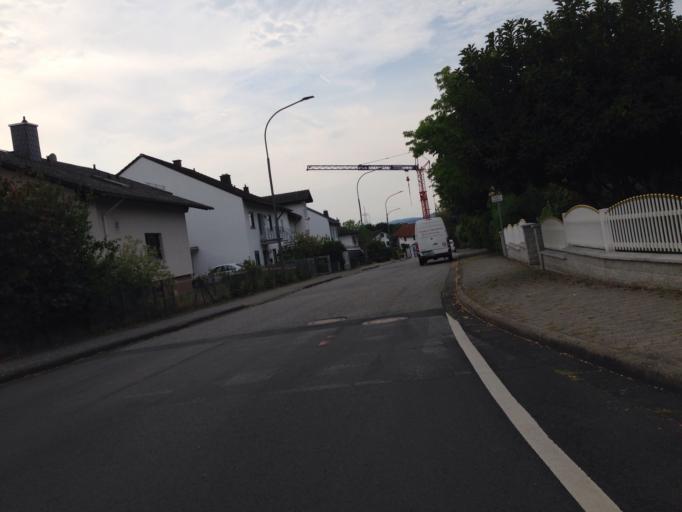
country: DE
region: Hesse
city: Allendorf an der Lahn
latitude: 50.5564
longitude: 8.6422
